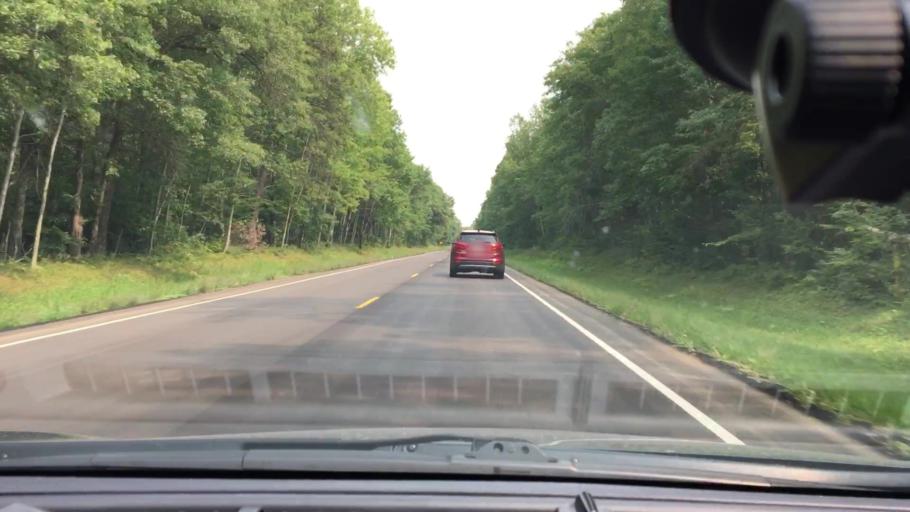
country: US
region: Minnesota
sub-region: Crow Wing County
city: Breezy Point
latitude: 46.5336
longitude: -94.1700
